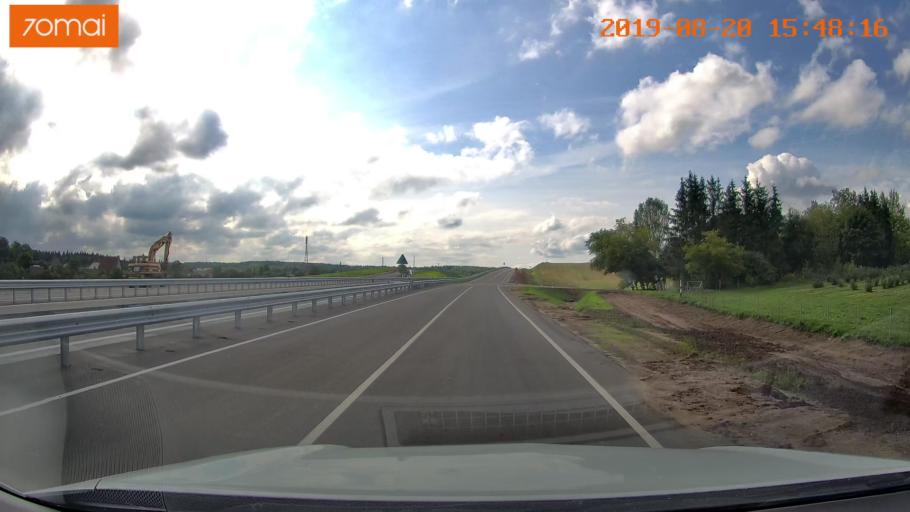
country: BY
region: Minsk
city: Slabada
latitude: 54.0343
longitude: 27.8549
